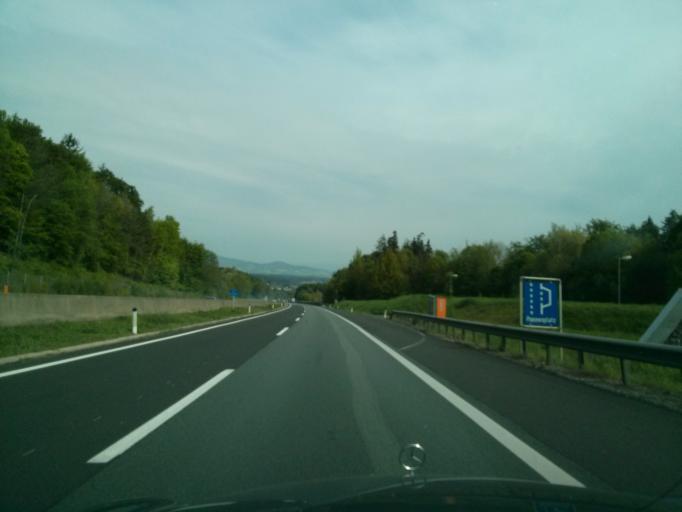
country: AT
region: Styria
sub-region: Politischer Bezirk Hartberg-Fuerstenfeld
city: Bad Waltersdorf
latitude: 47.1627
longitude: 16.0012
